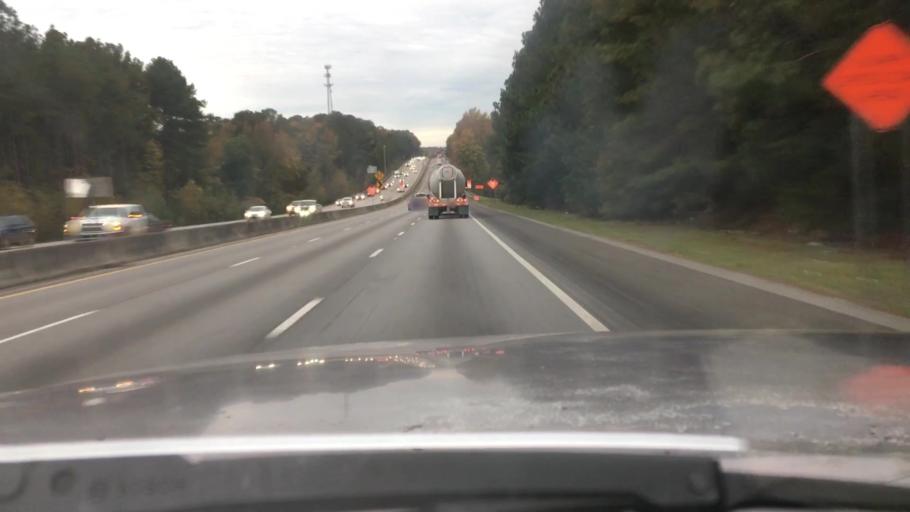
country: US
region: South Carolina
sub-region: Lexington County
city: Oak Grove
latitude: 34.0078
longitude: -81.1576
